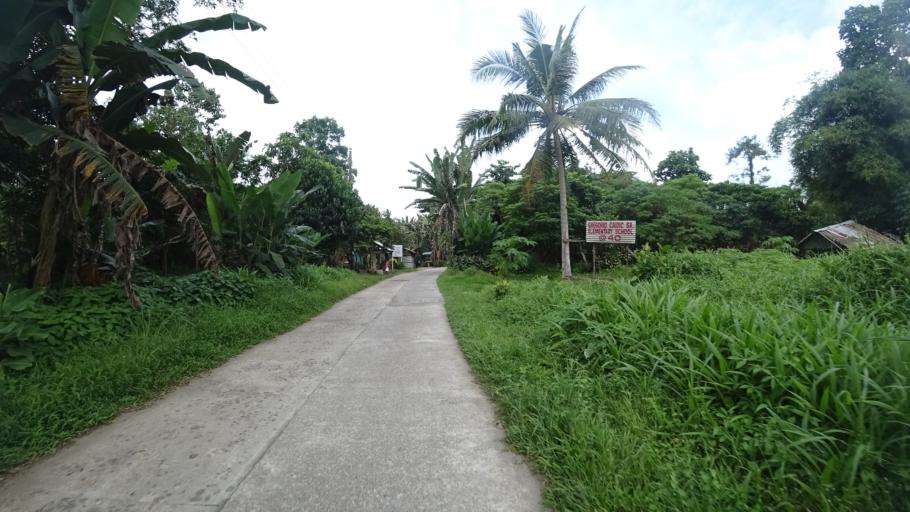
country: PH
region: Eastern Visayas
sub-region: Province of Leyte
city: Alangalang
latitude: 11.1724
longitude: 124.8677
